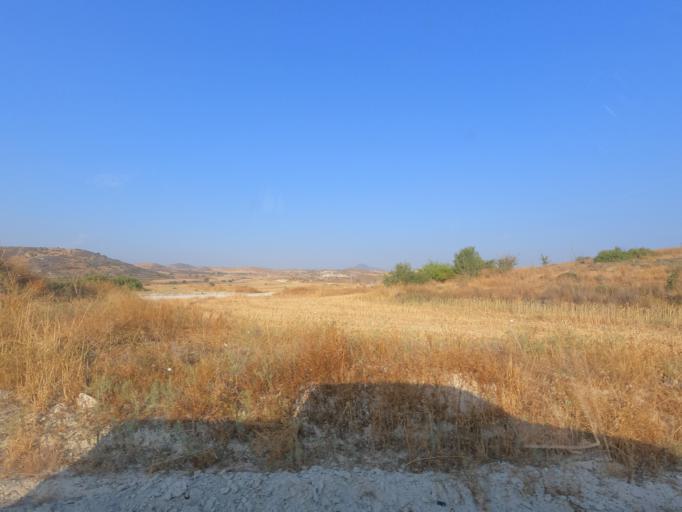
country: CY
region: Larnaka
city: Psevdas
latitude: 34.9186
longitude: 33.5138
